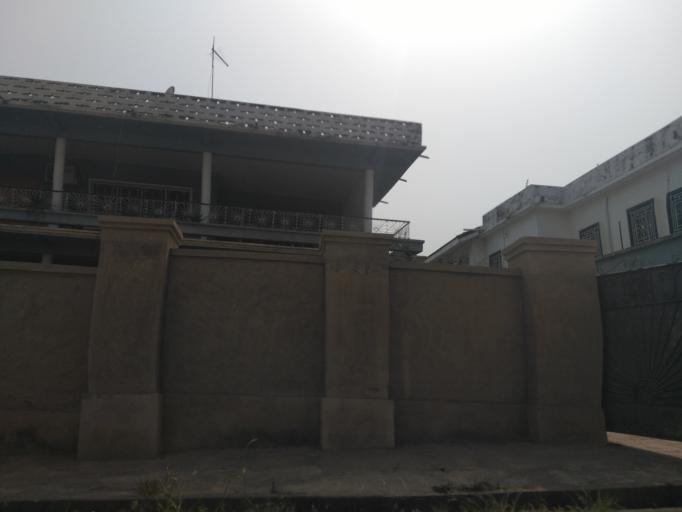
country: GH
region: Ashanti
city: Kumasi
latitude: 6.6806
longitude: -1.6017
